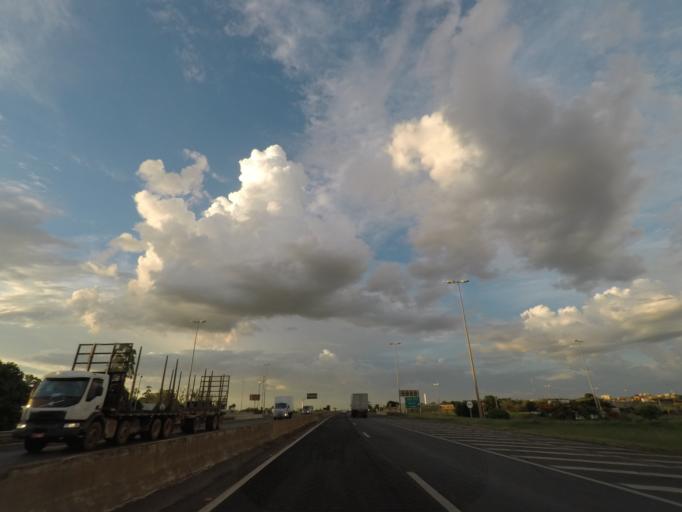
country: BR
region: Minas Gerais
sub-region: Uberaba
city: Uberaba
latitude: -19.7766
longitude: -47.9715
